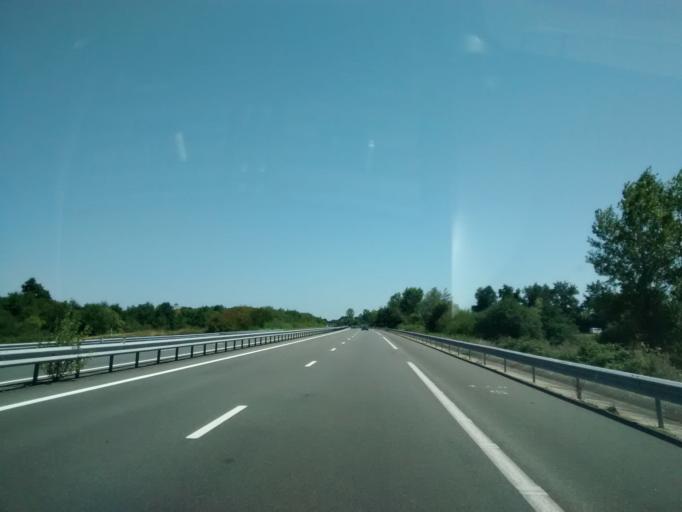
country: FR
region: Aquitaine
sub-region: Departement de la Gironde
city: Saint-Medard-de-Guizieres
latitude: 45.0069
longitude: -0.0651
